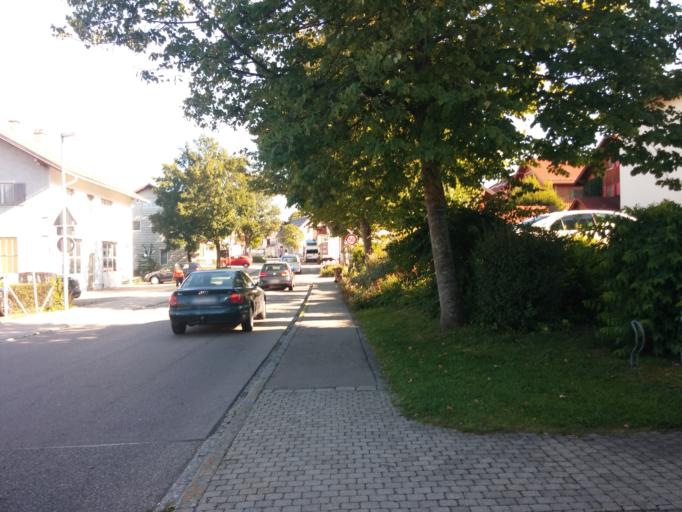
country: DE
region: Bavaria
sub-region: Swabia
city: Wiggensbach
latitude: 47.7475
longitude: 10.2288
